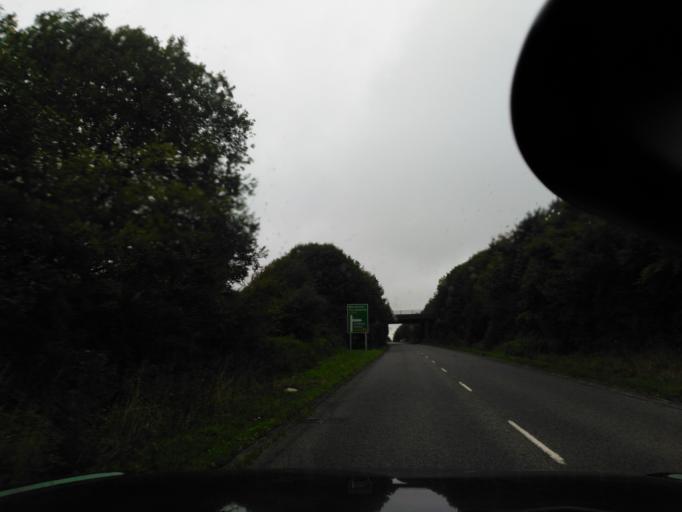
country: GB
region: England
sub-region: Wiltshire
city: Chicklade
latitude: 51.1038
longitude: -2.1649
